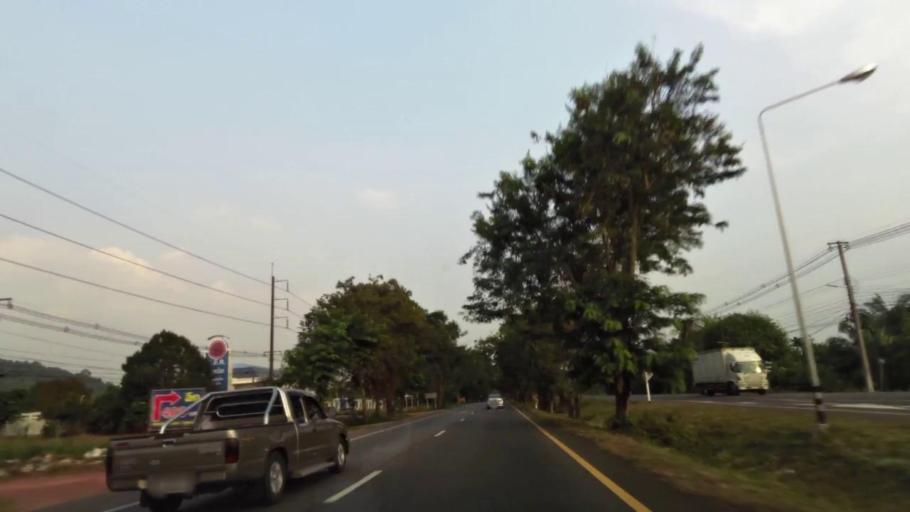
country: TH
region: Chanthaburi
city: Khlung
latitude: 12.4653
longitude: 102.2098
